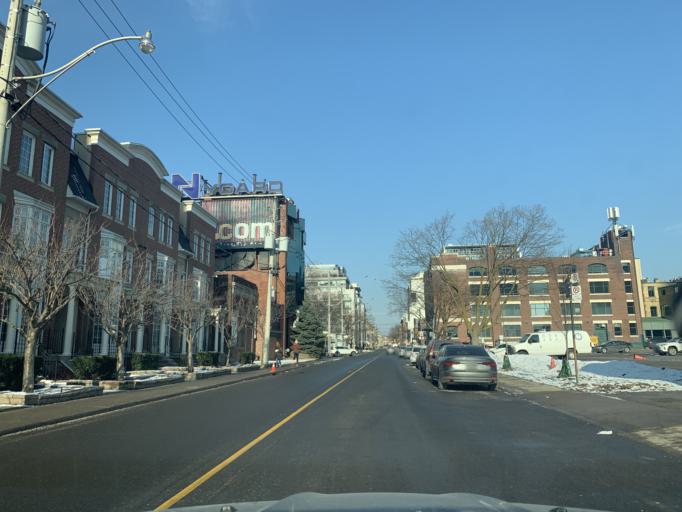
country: CA
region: Ontario
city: Toronto
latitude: 43.6418
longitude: -79.3990
